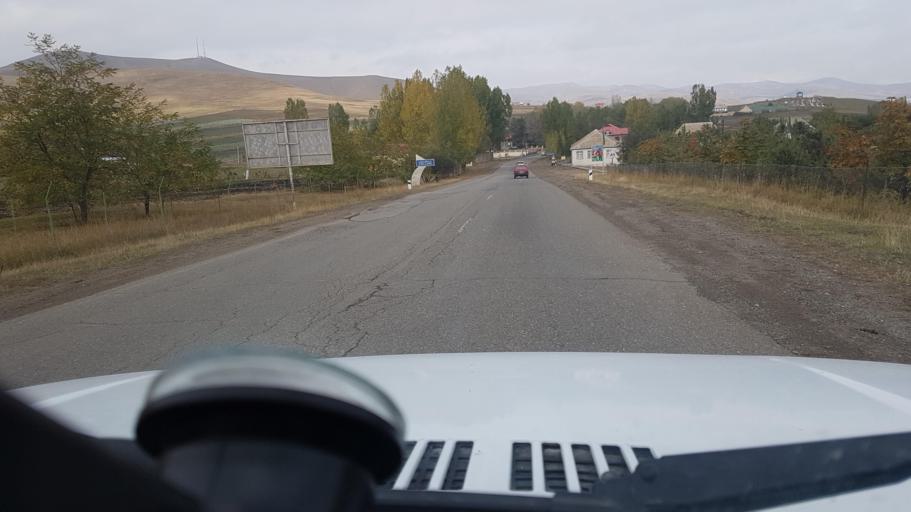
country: AZ
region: Gadabay Rayon
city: Ariqdam
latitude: 40.6316
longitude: 45.8140
